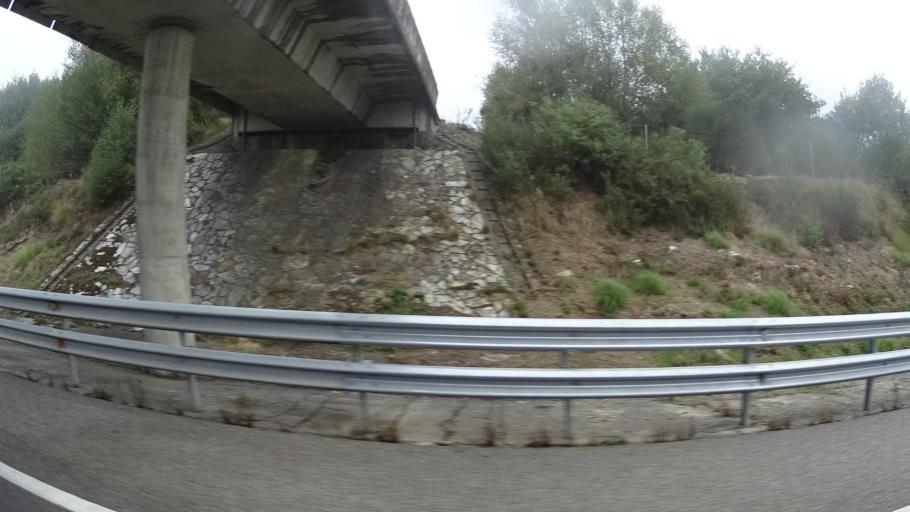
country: ES
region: Galicia
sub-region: Provincia de Lugo
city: Guitiriz
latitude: 43.1871
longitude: -7.8438
